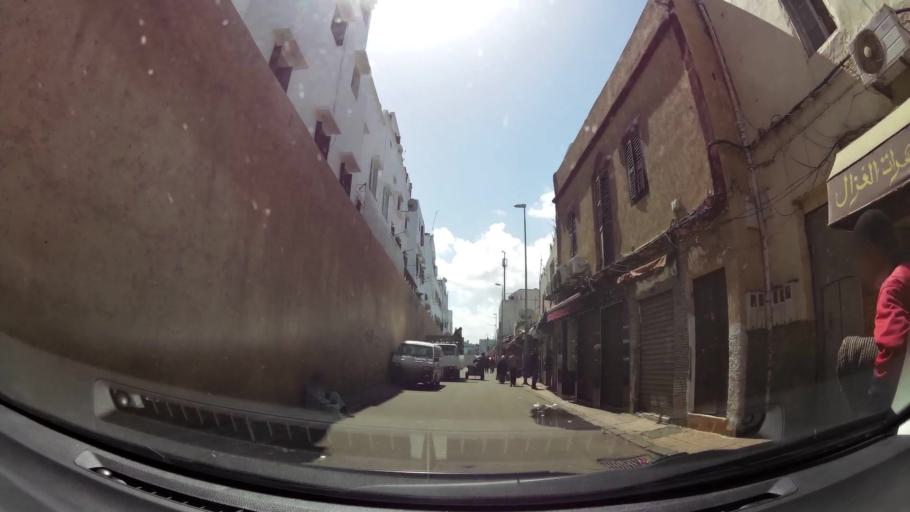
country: MA
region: Grand Casablanca
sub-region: Casablanca
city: Casablanca
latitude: 33.5990
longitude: -7.6222
